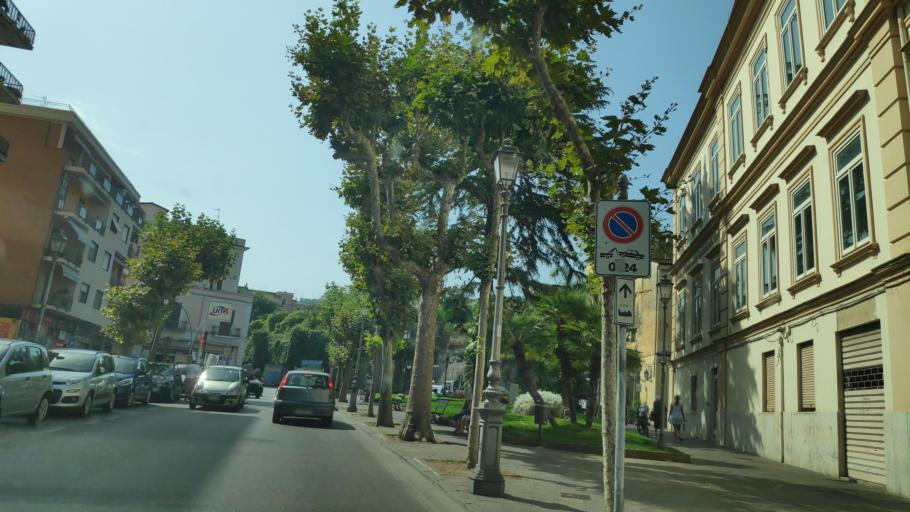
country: IT
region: Campania
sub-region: Provincia di Napoli
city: Sant'Agnello
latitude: 40.6309
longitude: 14.3992
